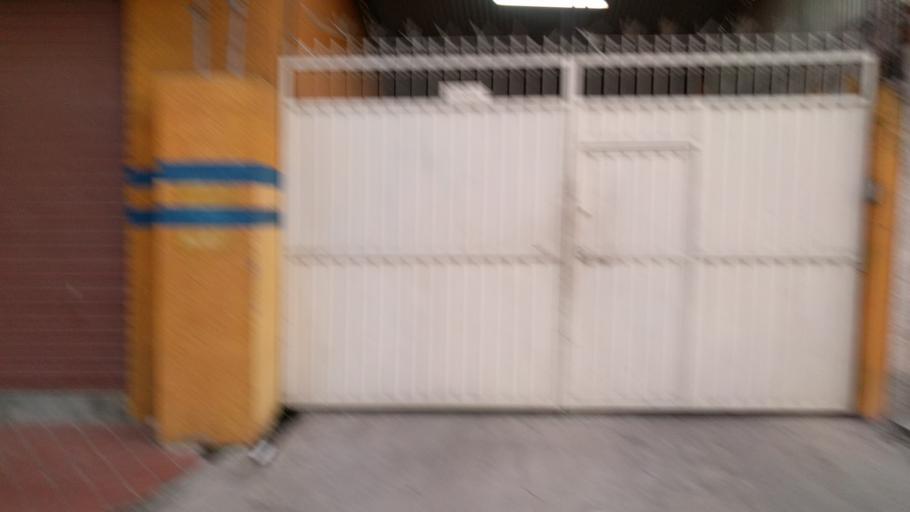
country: BO
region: Santa Cruz
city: Santa Cruz de la Sierra
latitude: -17.7696
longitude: -63.1588
